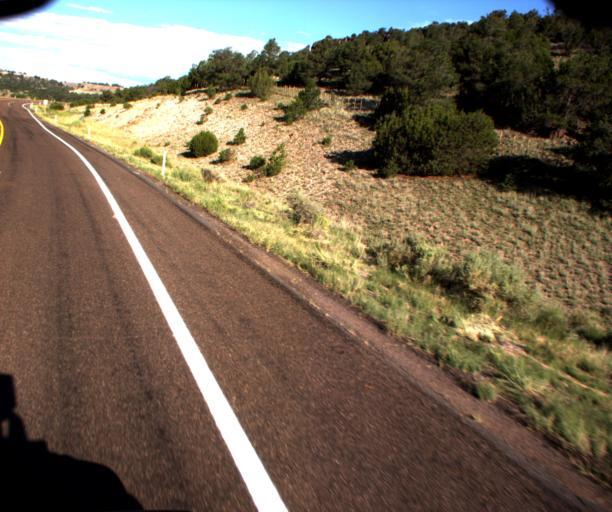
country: US
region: Arizona
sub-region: Apache County
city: Eagar
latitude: 34.0927
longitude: -109.2059
